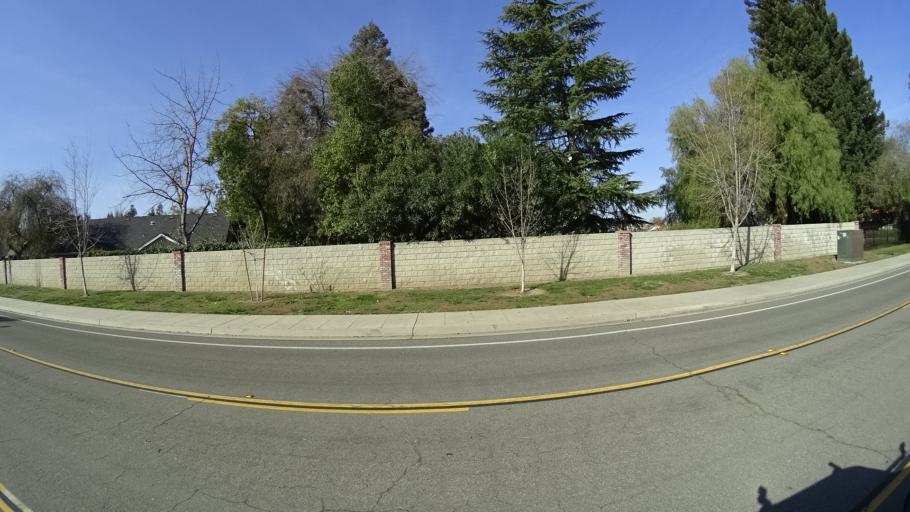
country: US
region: California
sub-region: Fresno County
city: Clovis
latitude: 36.8861
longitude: -119.7676
